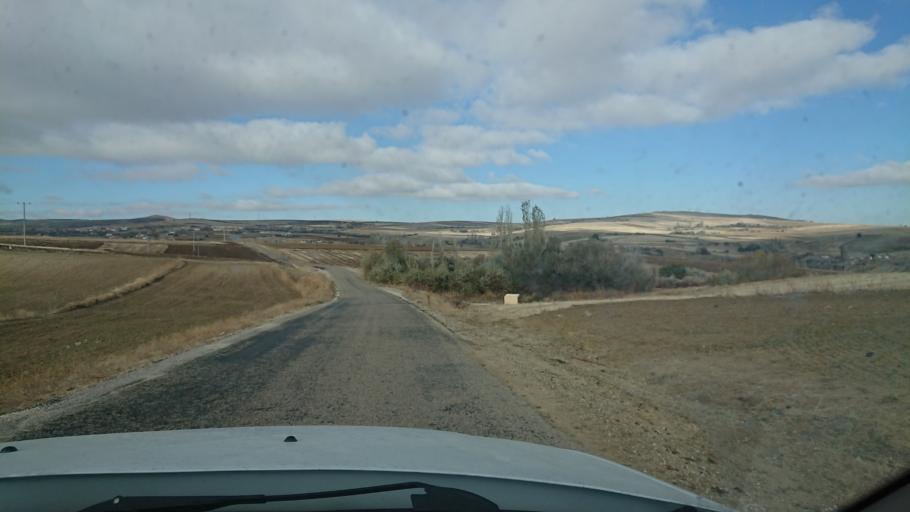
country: TR
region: Aksaray
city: Agacoren
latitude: 38.8185
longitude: 33.9783
